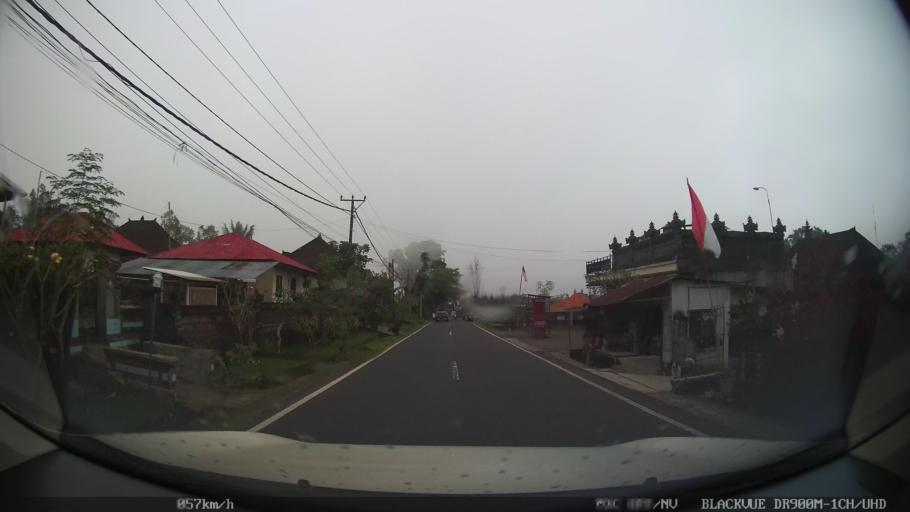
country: ID
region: Bali
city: Banjar Kedisan
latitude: -8.3061
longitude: 115.3063
